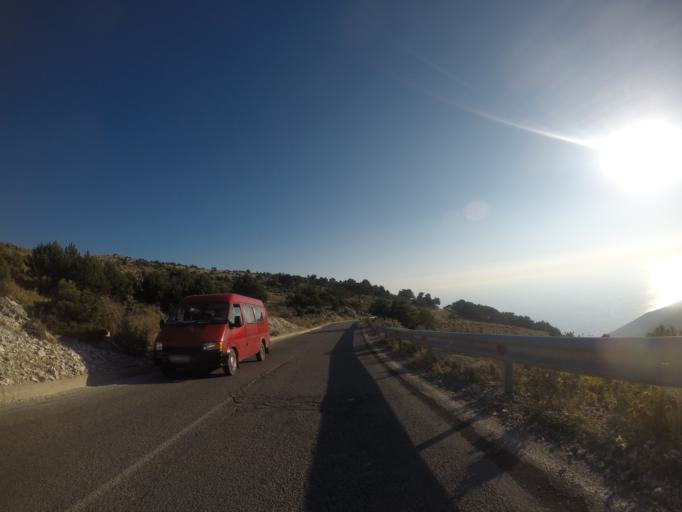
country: AL
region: Vlore
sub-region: Rrethi i Vlores
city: Vranisht
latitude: 40.1919
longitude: 19.5998
